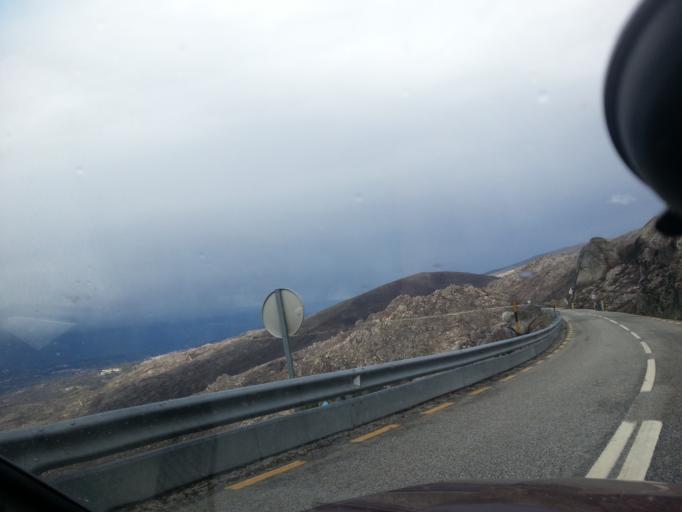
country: PT
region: Guarda
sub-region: Manteigas
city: Manteigas
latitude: 40.4280
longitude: -7.6102
